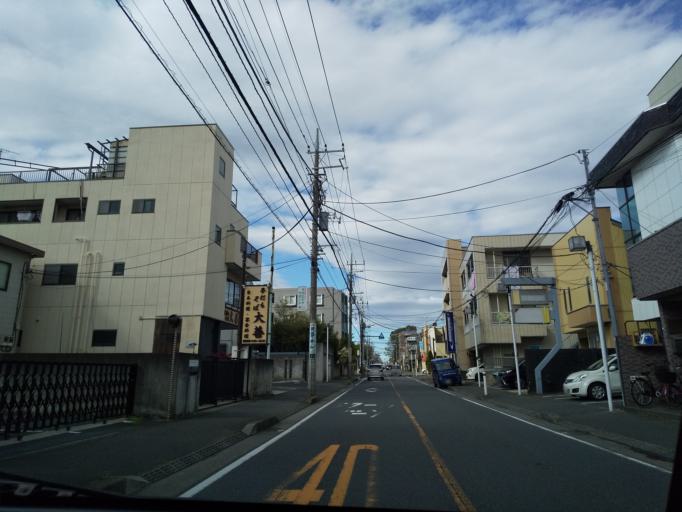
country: JP
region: Kanagawa
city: Zama
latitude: 35.5671
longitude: 139.3761
